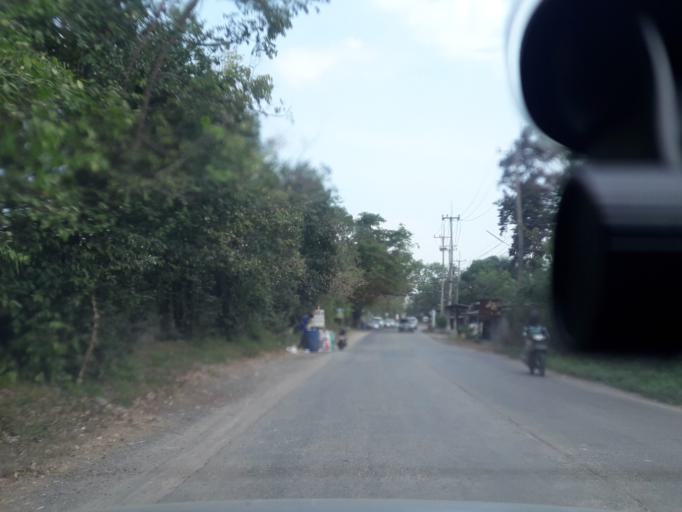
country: TH
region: Sara Buri
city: Nong Khae
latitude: 14.3281
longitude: 100.8722
